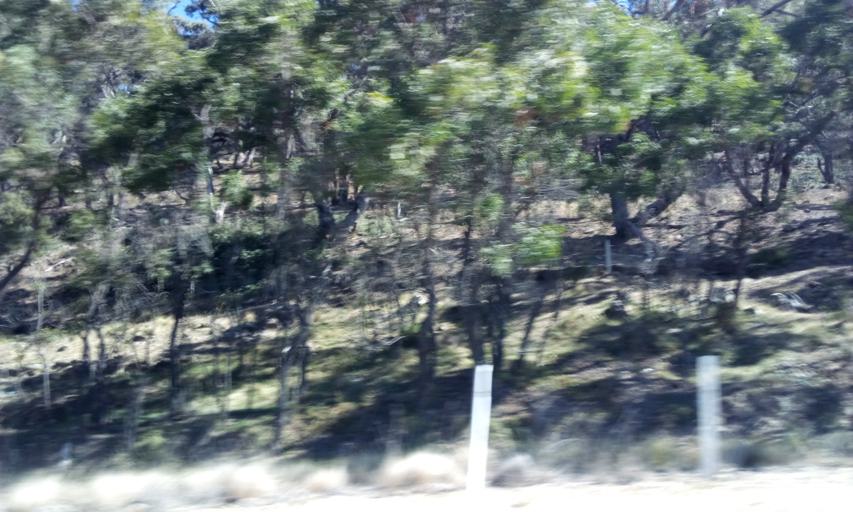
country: AU
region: New South Wales
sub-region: Yass Valley
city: Gundaroo
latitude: -35.0949
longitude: 149.3762
